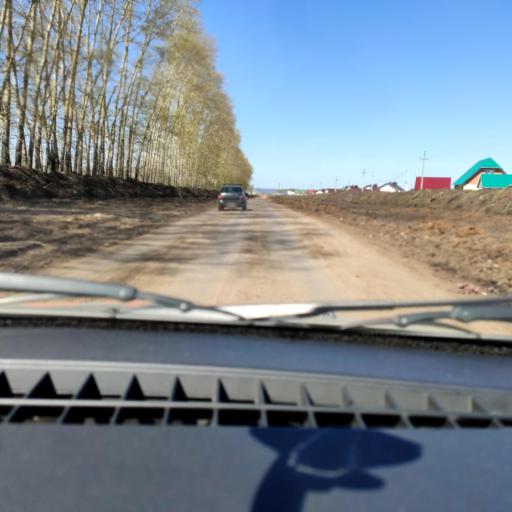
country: RU
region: Bashkortostan
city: Iglino
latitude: 54.8148
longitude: 56.4349
